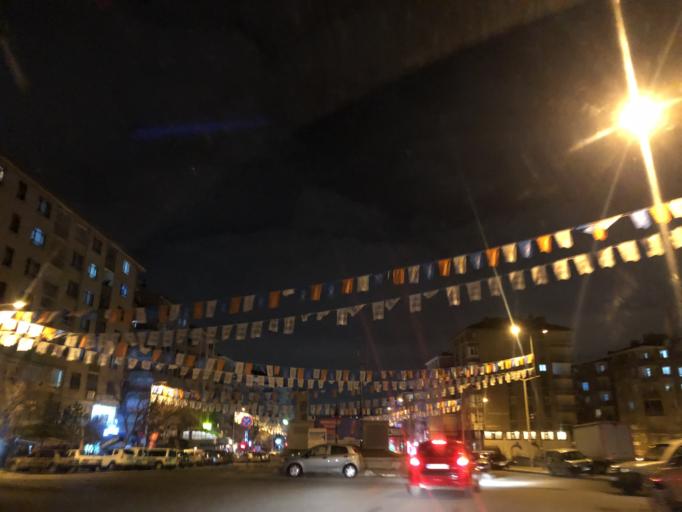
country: TR
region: Ankara
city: Batikent
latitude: 39.9696
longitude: 32.7822
